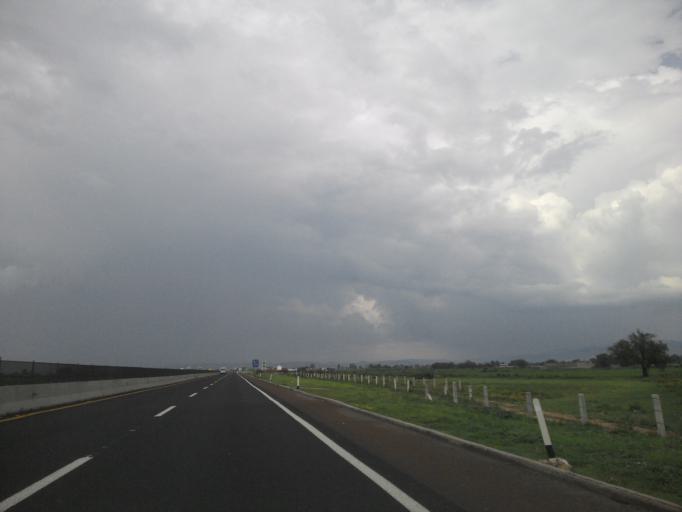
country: MX
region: Hidalgo
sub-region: Tula de Allende
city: Residencial Arboledas
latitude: 20.0921
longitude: -99.3061
